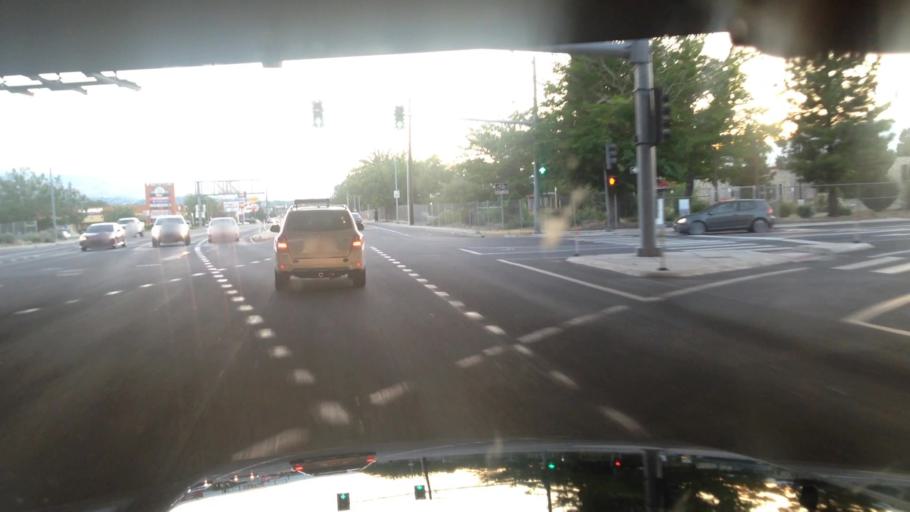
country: US
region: Nevada
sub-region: Washoe County
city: Sparks
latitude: 39.5060
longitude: -119.7805
